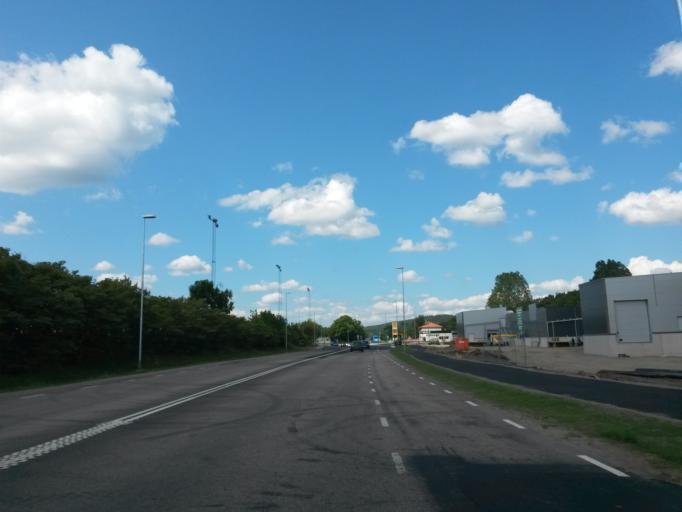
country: SE
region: Vaestra Goetaland
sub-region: Alingsas Kommun
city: Alingsas
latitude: 57.9390
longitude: 12.5291
